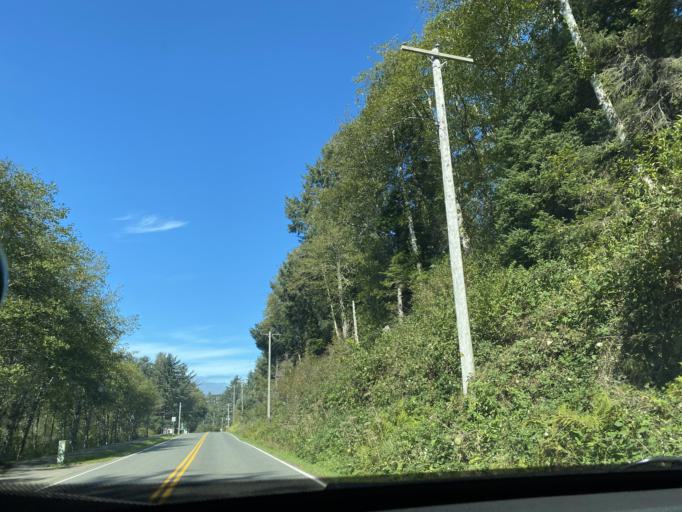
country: US
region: Washington
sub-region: Clallam County
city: Forks
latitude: 47.9028
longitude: -124.6281
